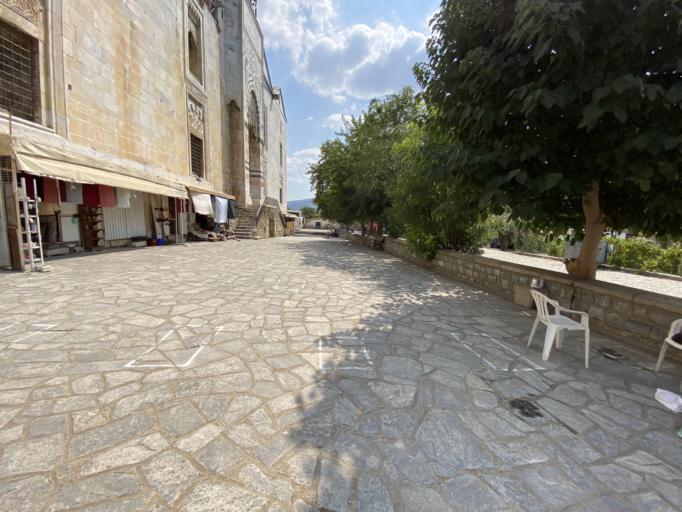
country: TR
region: Izmir
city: Selcuk
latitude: 37.9526
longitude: 27.3657
